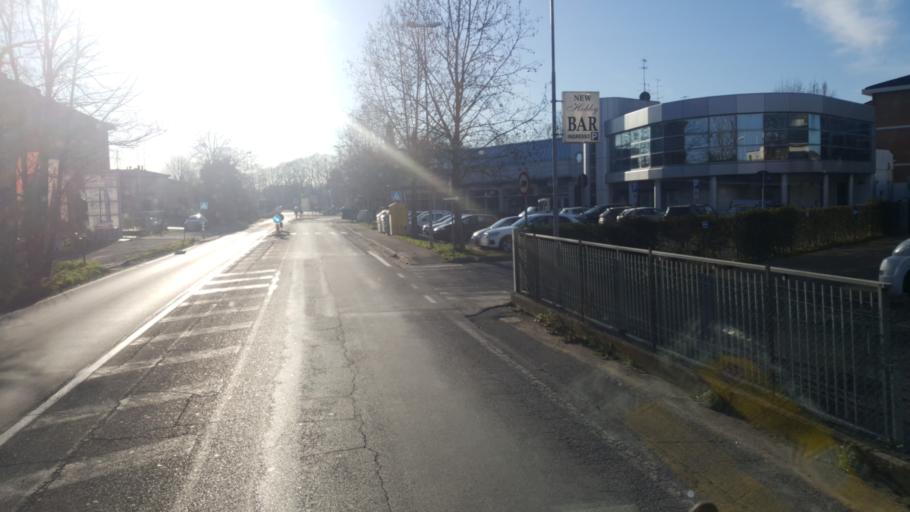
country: IT
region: Emilia-Romagna
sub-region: Provincia di Reggio Emilia
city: Rubiera
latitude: 44.6538
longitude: 10.7862
